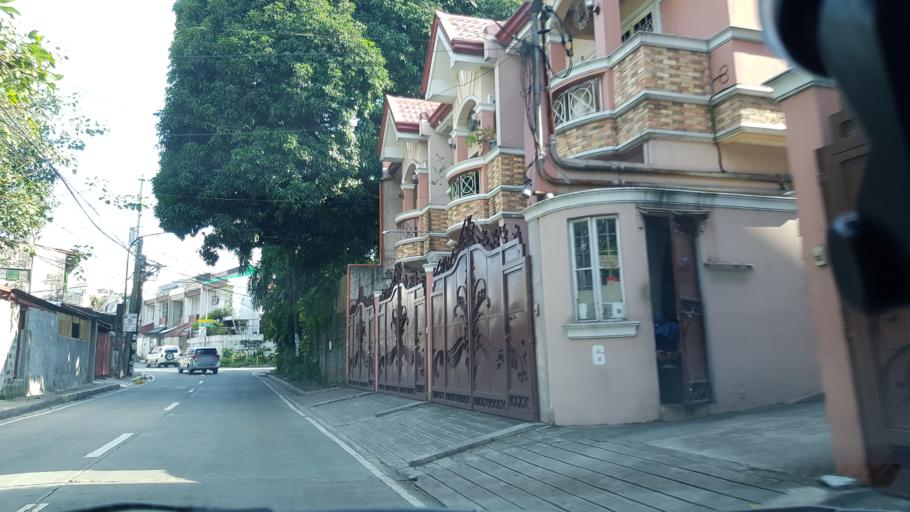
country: PH
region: Metro Manila
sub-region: San Juan
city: San Juan
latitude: 14.6240
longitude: 121.0376
